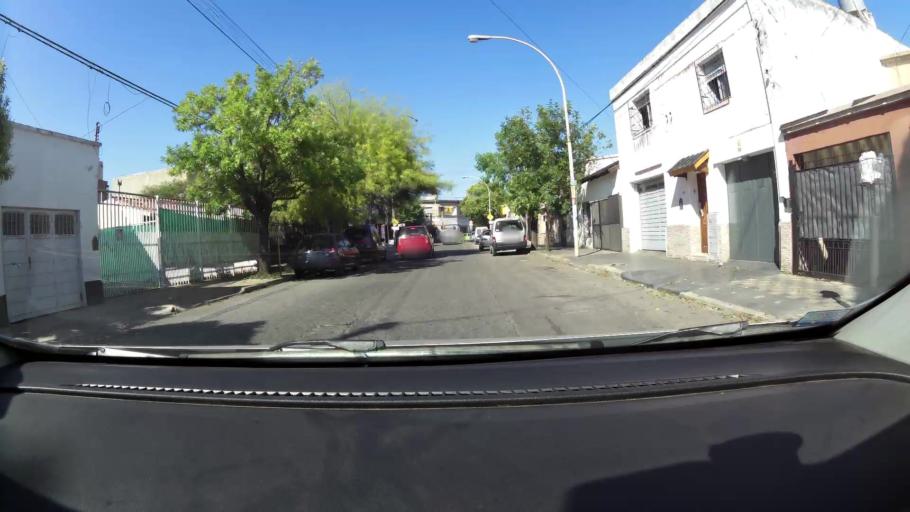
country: AR
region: Cordoba
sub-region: Departamento de Capital
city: Cordoba
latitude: -31.4392
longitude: -64.1611
